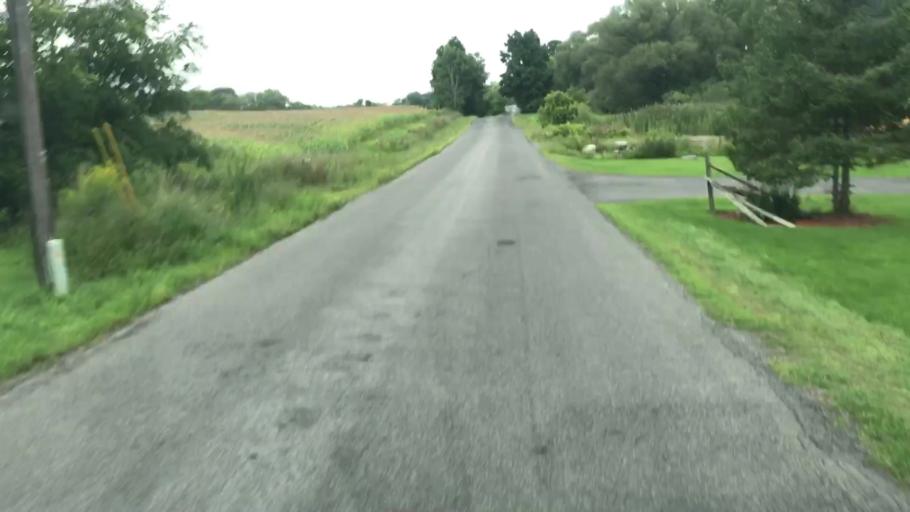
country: US
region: New York
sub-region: Cayuga County
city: Melrose Park
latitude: 42.9610
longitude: -76.5070
